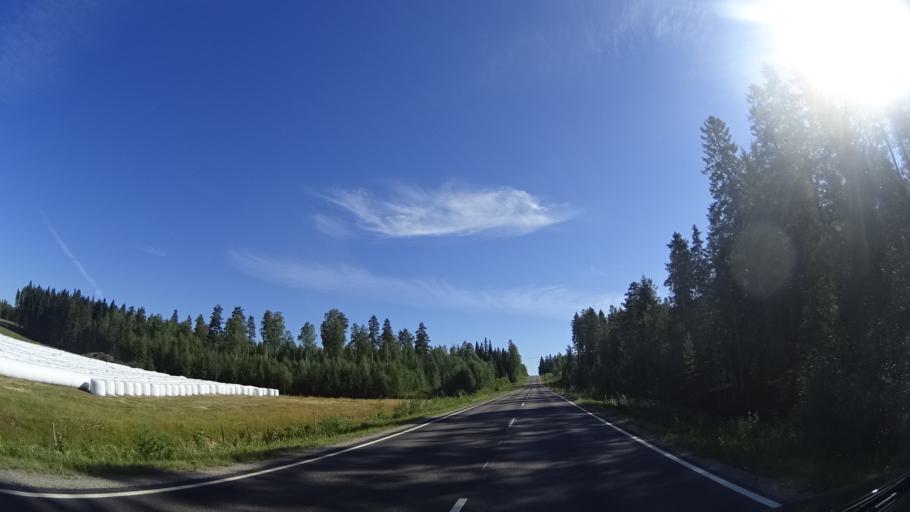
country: FI
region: Central Finland
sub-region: Jyvaeskylae
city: Uurainen
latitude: 62.4804
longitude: 25.4189
